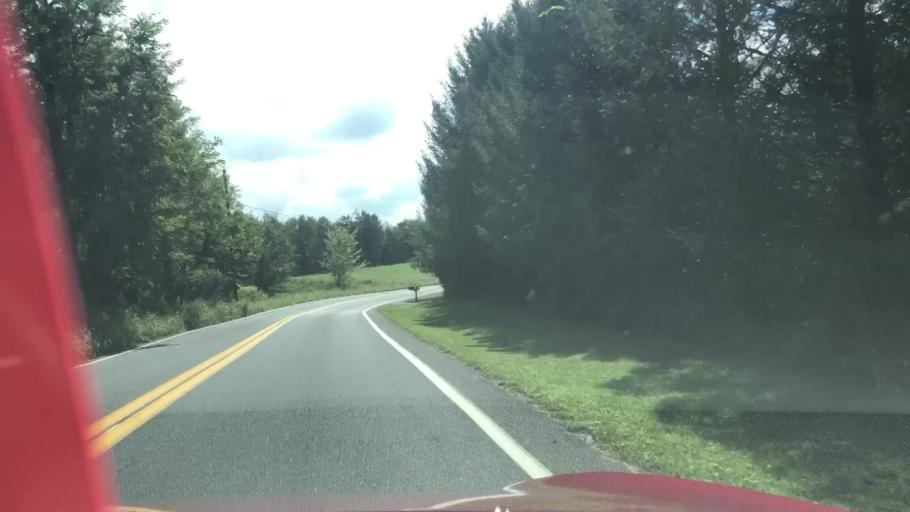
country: US
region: Pennsylvania
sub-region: Dauphin County
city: Skyline View
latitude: 40.3554
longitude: -76.6712
